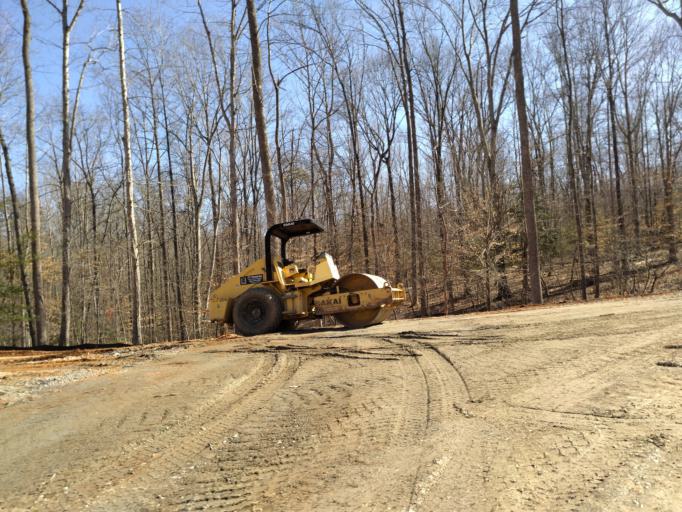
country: US
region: Virginia
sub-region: Chesterfield County
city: Chesterfield
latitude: 37.3825
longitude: -77.5584
